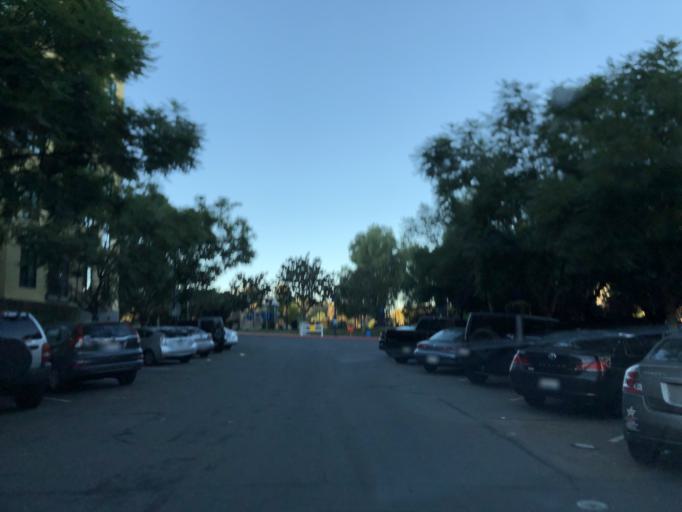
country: US
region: California
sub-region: San Diego County
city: San Diego
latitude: 32.7225
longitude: -117.1566
